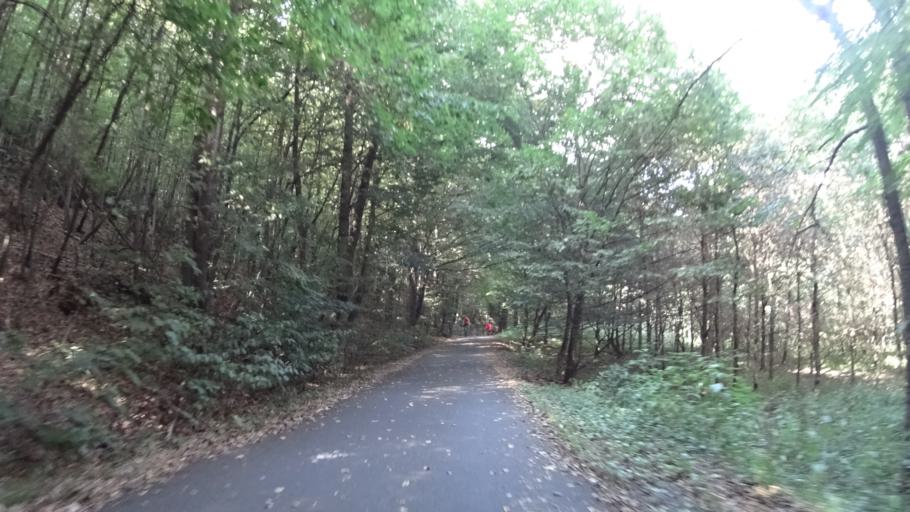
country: DE
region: Saxony
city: Schlegel
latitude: 50.9679
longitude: 14.9034
